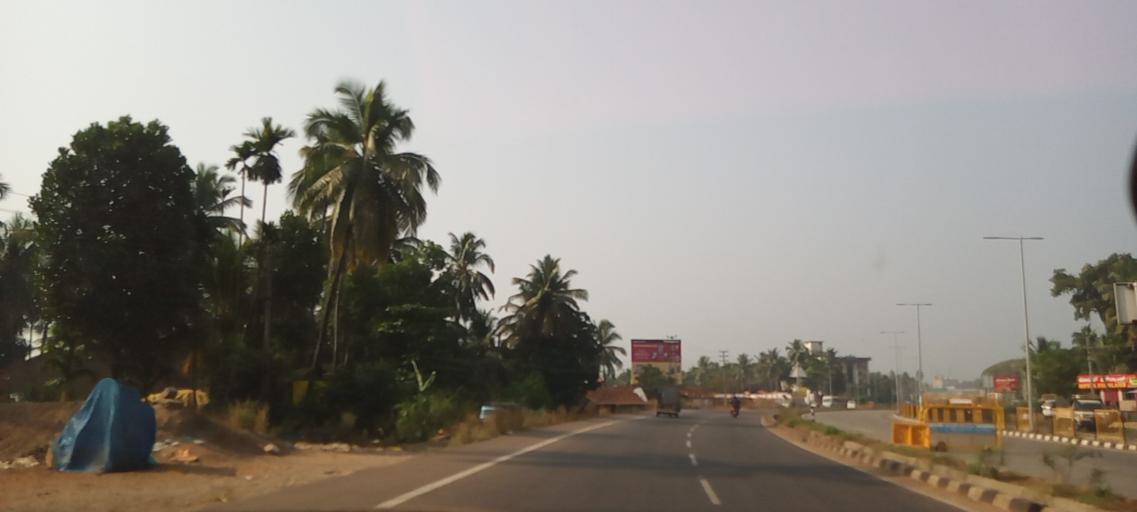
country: IN
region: Karnataka
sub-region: Udupi
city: Coondapoor
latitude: 13.6330
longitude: 74.7012
